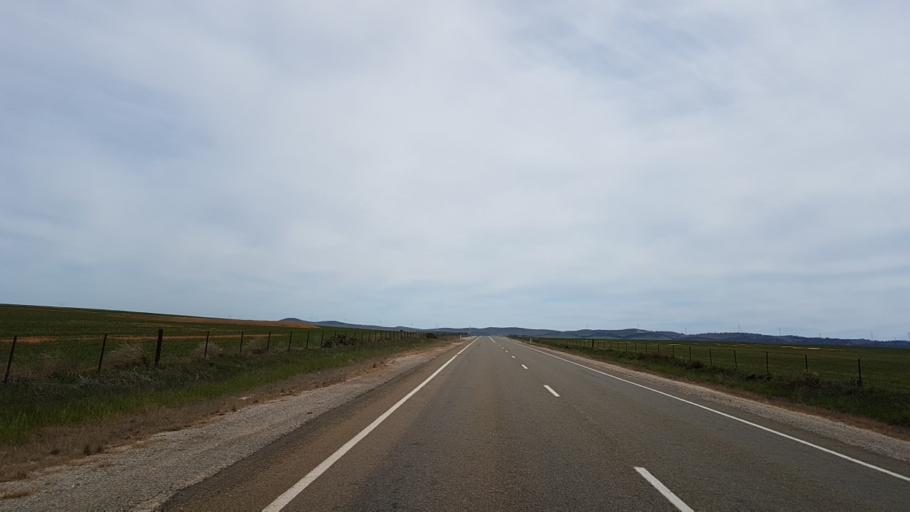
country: AU
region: South Australia
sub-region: Peterborough
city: Peterborough
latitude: -33.0243
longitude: 138.6750
